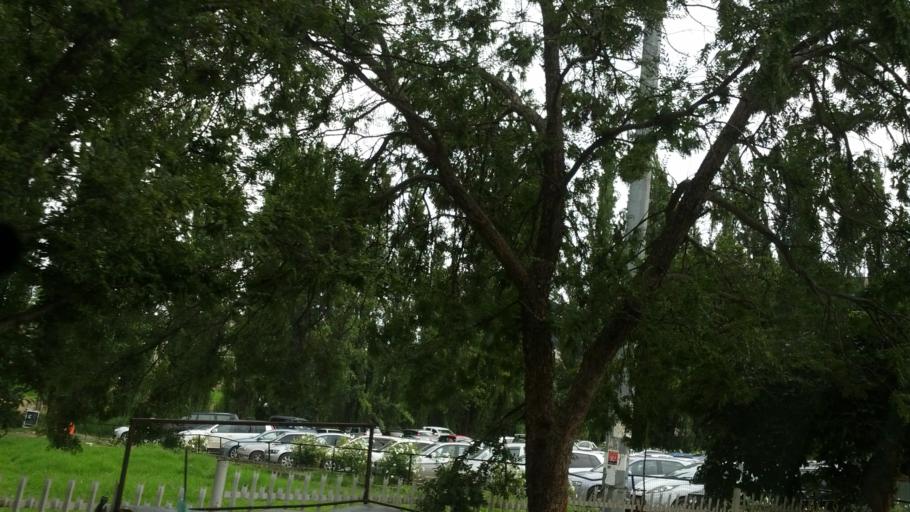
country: LS
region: Maseru
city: Maseru
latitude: -29.3159
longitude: 27.4818
